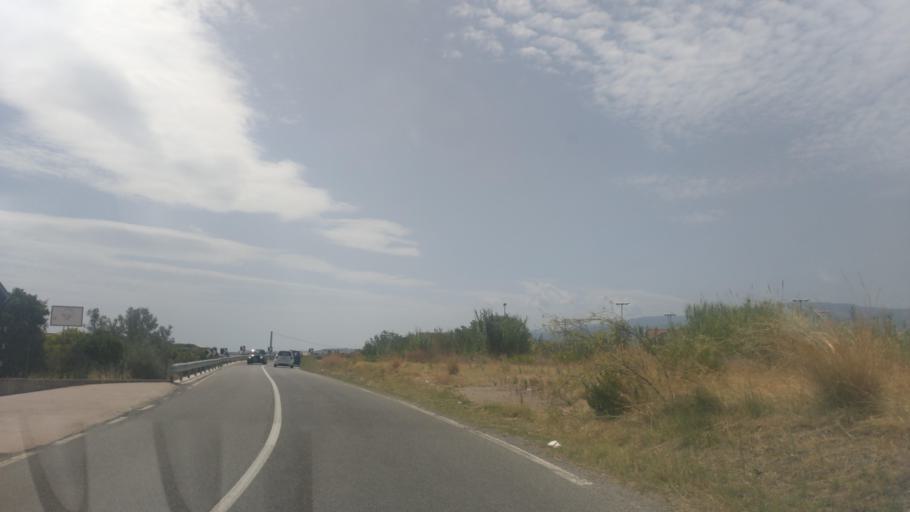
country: IT
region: Calabria
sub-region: Provincia di Catanzaro
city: Montepaone Lido
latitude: 38.7347
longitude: 16.5450
